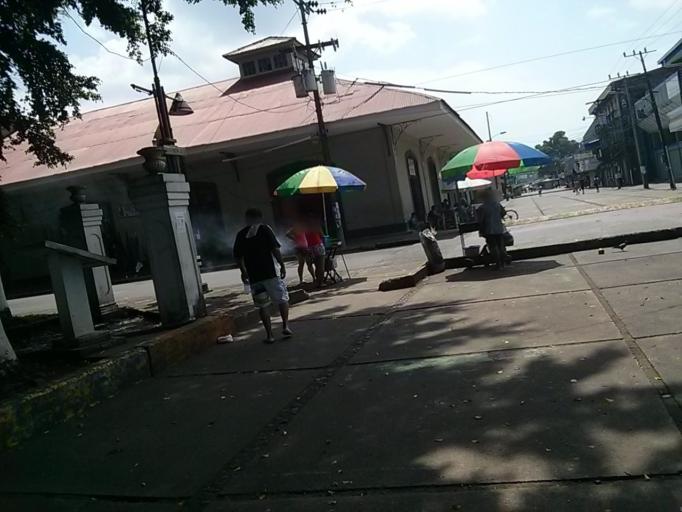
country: CR
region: Limon
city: Limon
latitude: 9.9929
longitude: -83.0259
